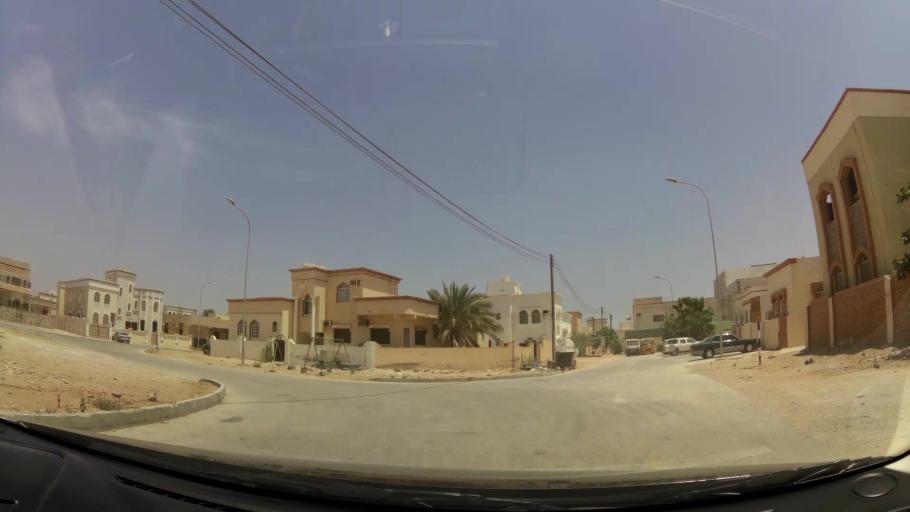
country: OM
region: Zufar
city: Salalah
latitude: 17.0783
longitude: 54.1501
